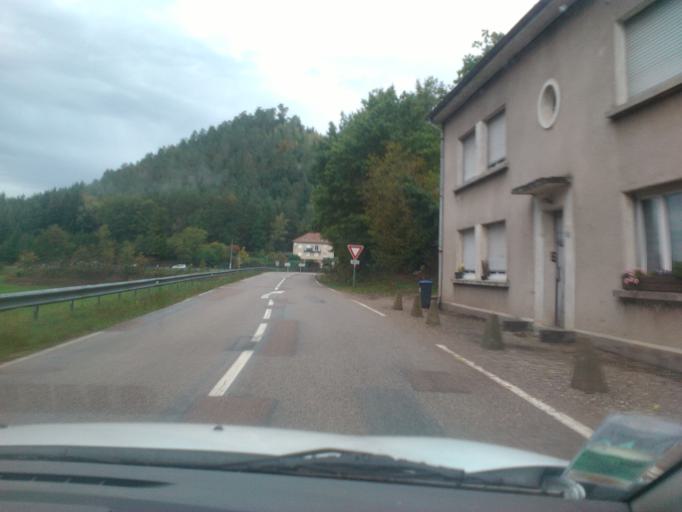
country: FR
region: Lorraine
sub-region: Departement des Vosges
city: Bruyeres
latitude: 48.2197
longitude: 6.7234
